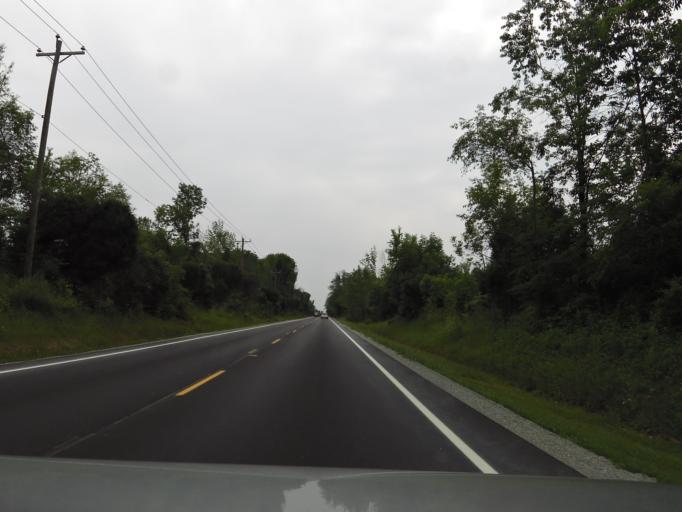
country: US
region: Ohio
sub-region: Clinton County
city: Blanchester
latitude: 39.2411
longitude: -83.9060
